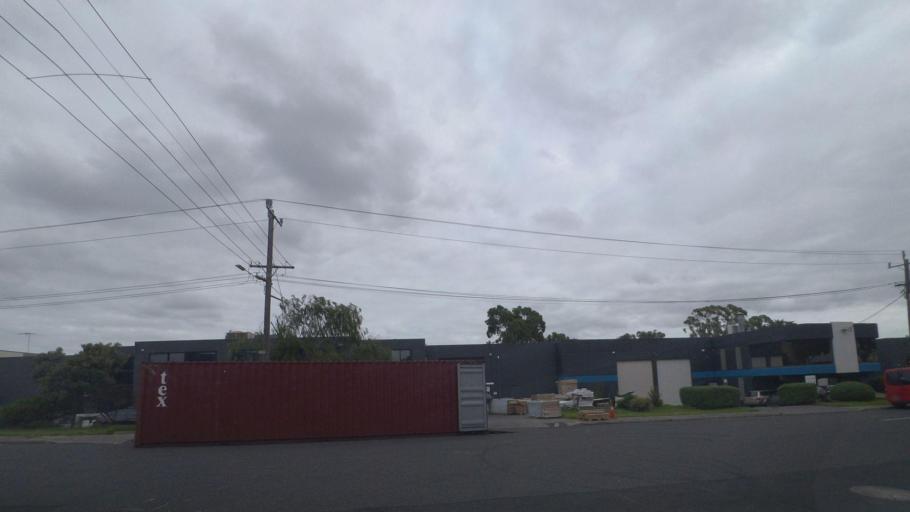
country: AU
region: Victoria
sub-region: Whitehorse
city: Nunawading
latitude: -37.8211
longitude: 145.1653
